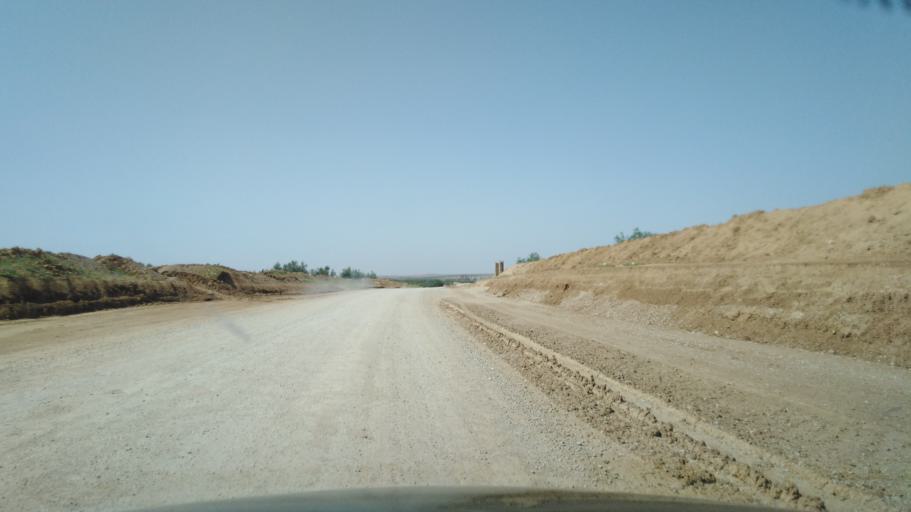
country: TN
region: Safaqis
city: Sfax
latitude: 34.7102
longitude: 10.4976
